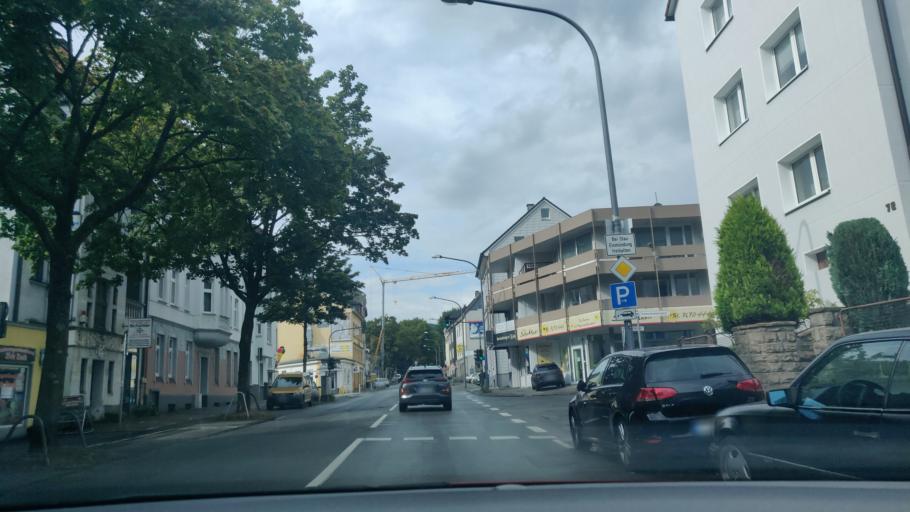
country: DE
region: North Rhine-Westphalia
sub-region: Regierungsbezirk Dusseldorf
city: Wuppertal
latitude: 51.2704
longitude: 7.1257
